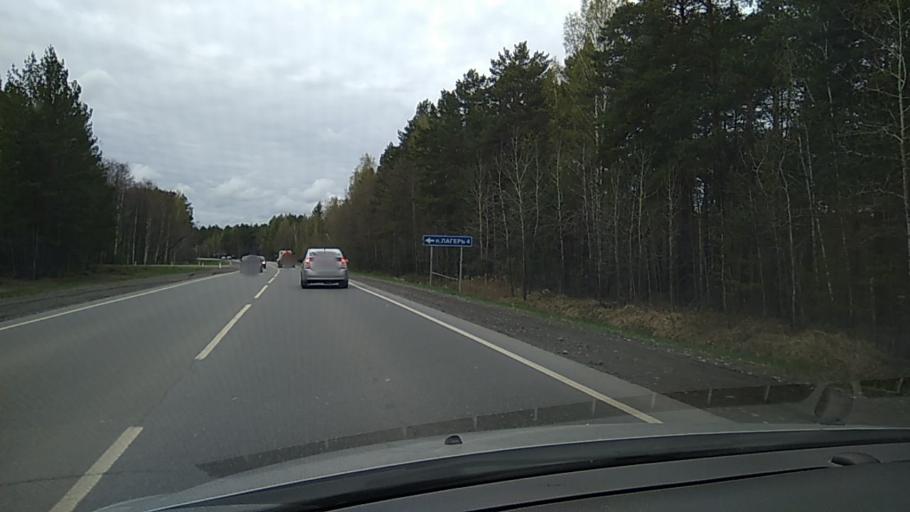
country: RU
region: Tjumen
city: Chervishevo
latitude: 56.9726
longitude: 65.4407
